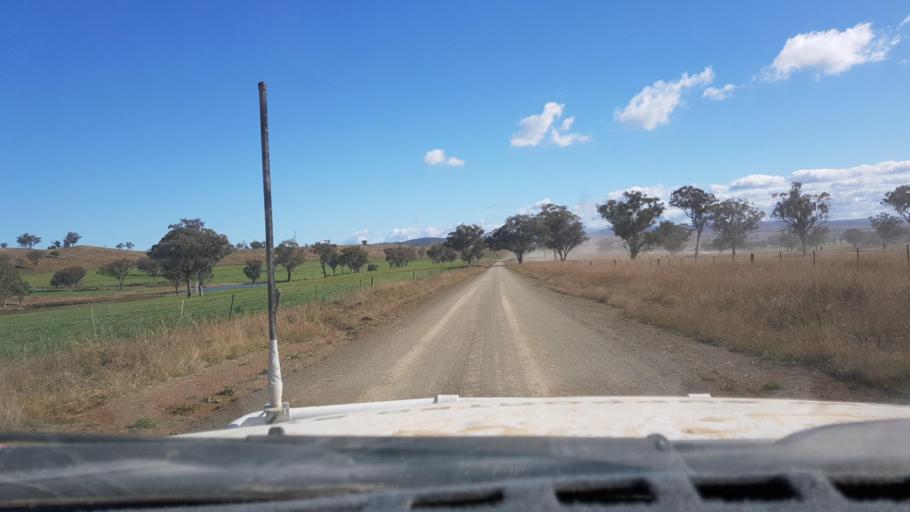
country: AU
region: New South Wales
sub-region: Narrabri
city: Blair Athol
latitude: -30.5467
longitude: 150.4560
